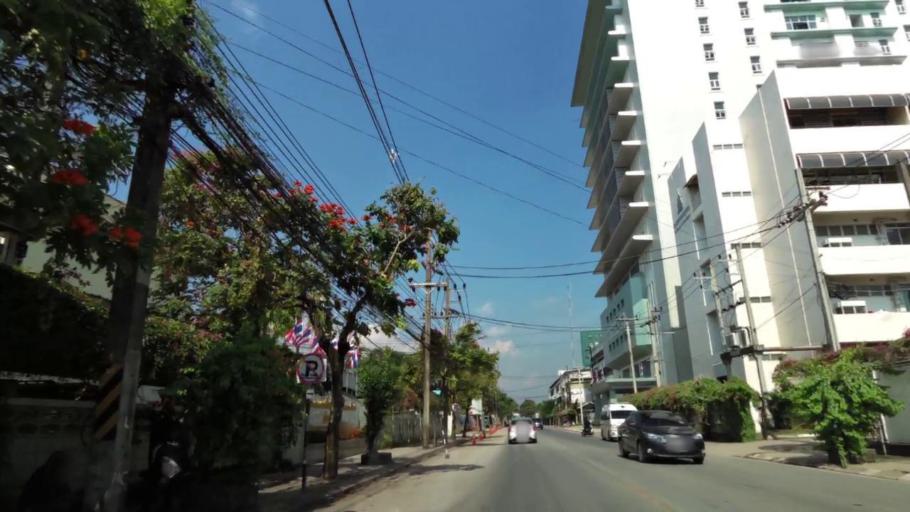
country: TH
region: Chiang Rai
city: Chiang Rai
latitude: 19.9000
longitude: 99.8280
